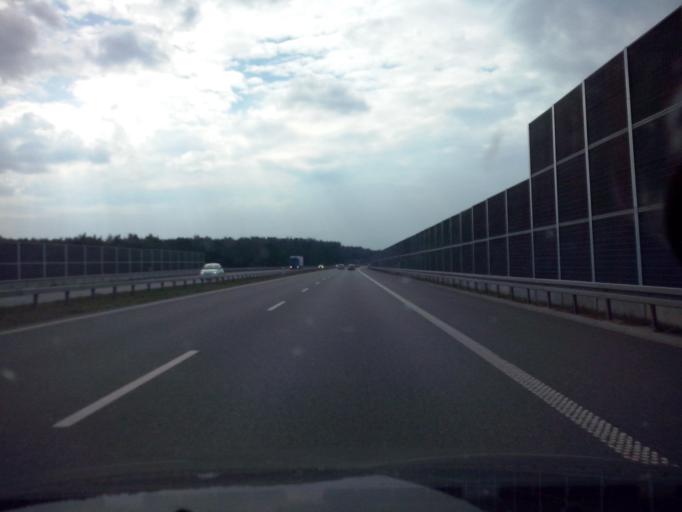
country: PL
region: Lesser Poland Voivodeship
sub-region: Powiat brzeski
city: Przyborow
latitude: 50.0027
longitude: 20.6578
